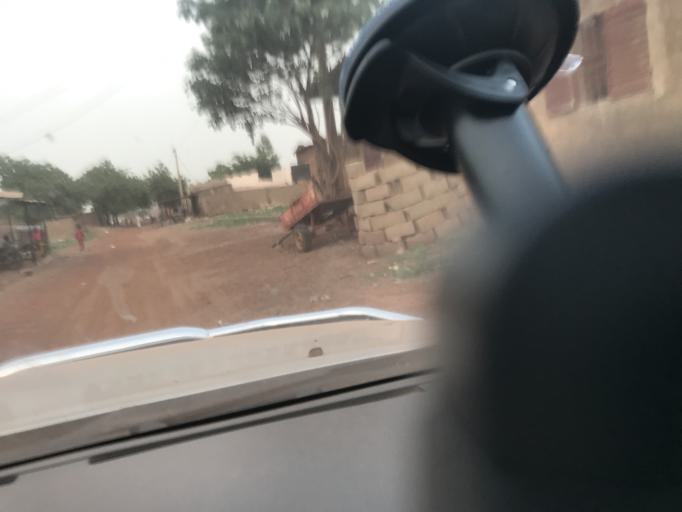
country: ML
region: Bamako
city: Bamako
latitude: 12.6530
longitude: -7.8891
